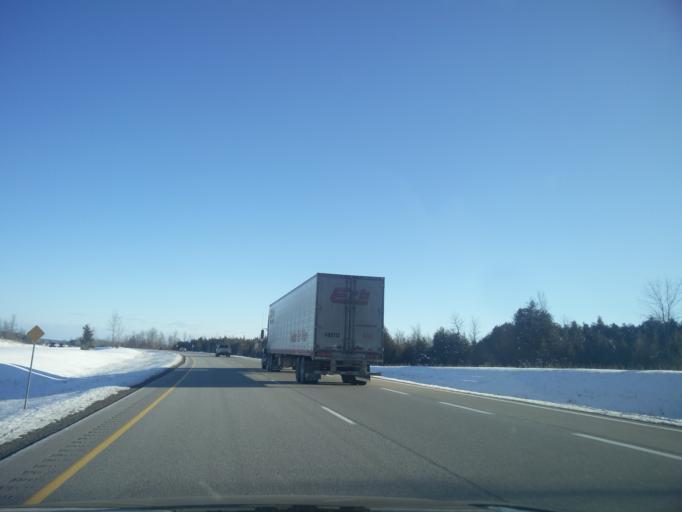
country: CA
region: Ontario
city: Prescott
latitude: 44.9802
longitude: -75.6097
